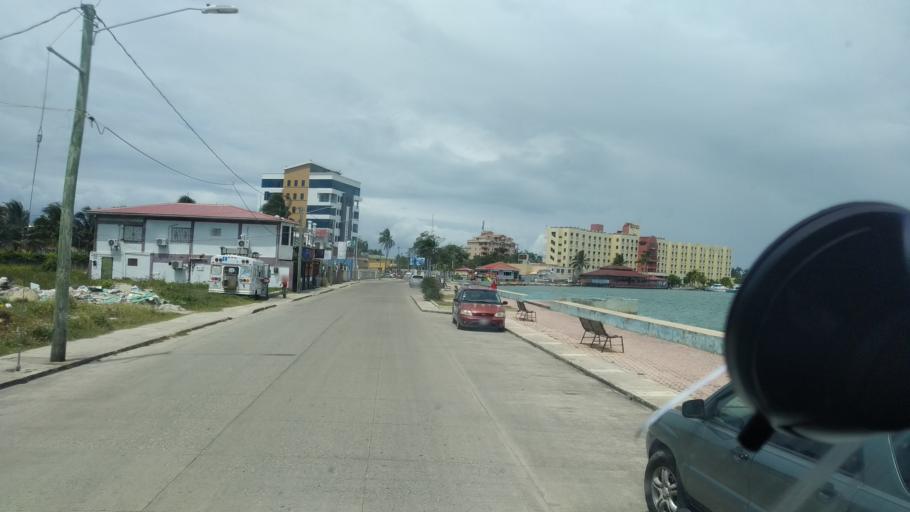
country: BZ
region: Belize
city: Belize City
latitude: 17.5021
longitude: -88.1868
